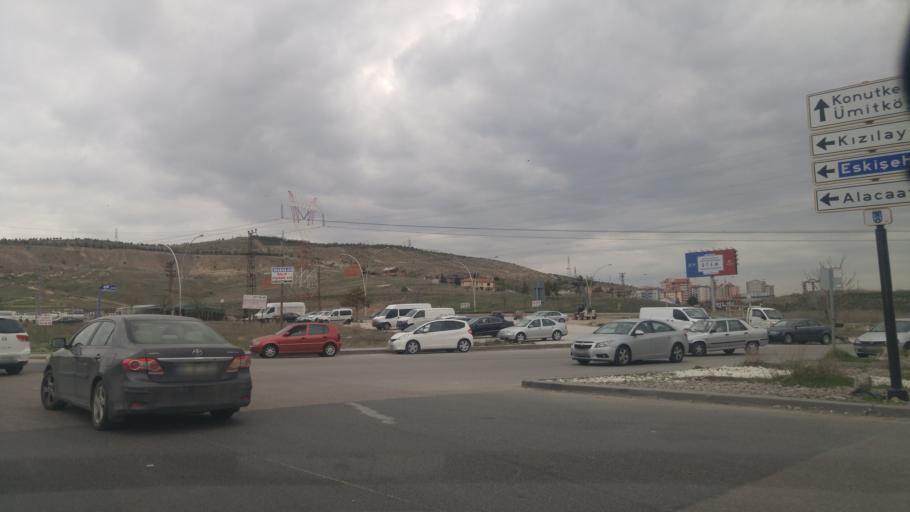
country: TR
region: Ankara
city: Etimesgut
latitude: 39.8705
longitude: 32.6447
